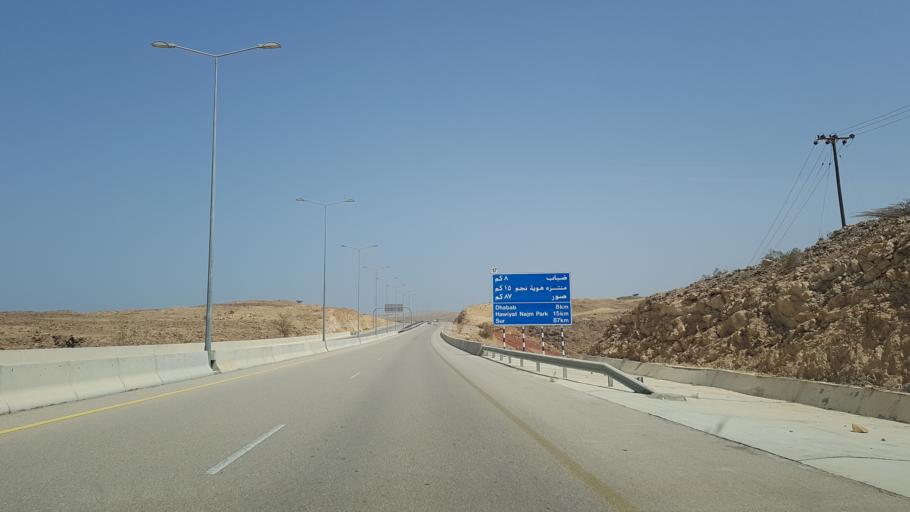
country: OM
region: Ash Sharqiyah
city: Al Qabil
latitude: 23.1042
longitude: 58.9879
